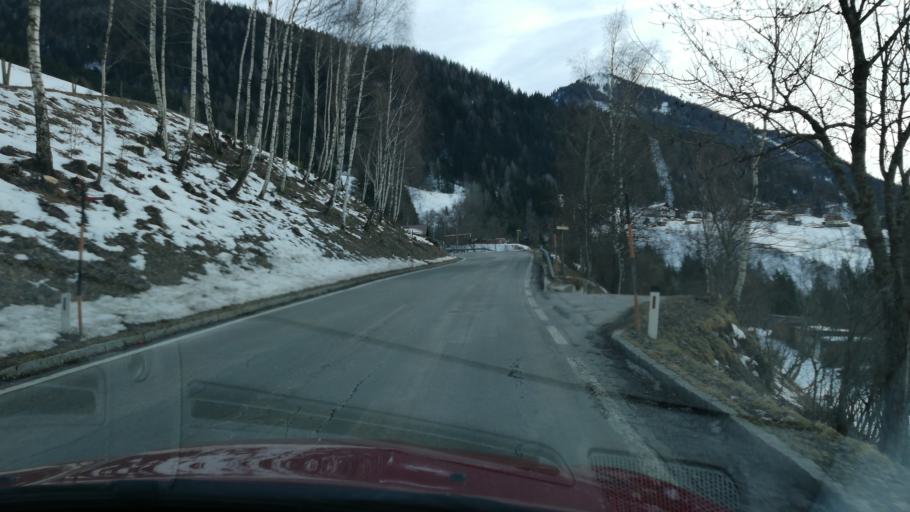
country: AT
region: Styria
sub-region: Politischer Bezirk Liezen
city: Donnersbach
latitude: 47.4498
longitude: 14.1422
